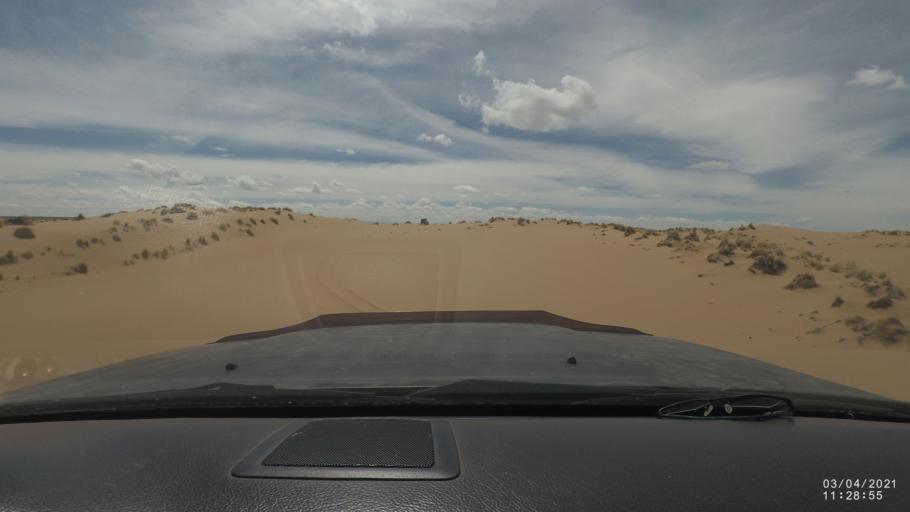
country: BO
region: Oruro
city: Poopo
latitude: -18.7029
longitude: -67.5096
